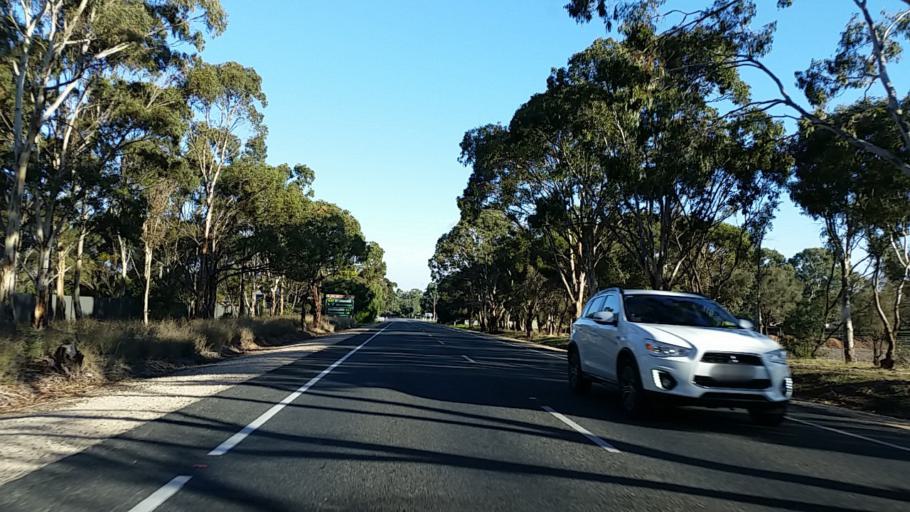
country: AU
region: South Australia
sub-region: Alexandrina
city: Strathalbyn
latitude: -35.2399
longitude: 138.8942
